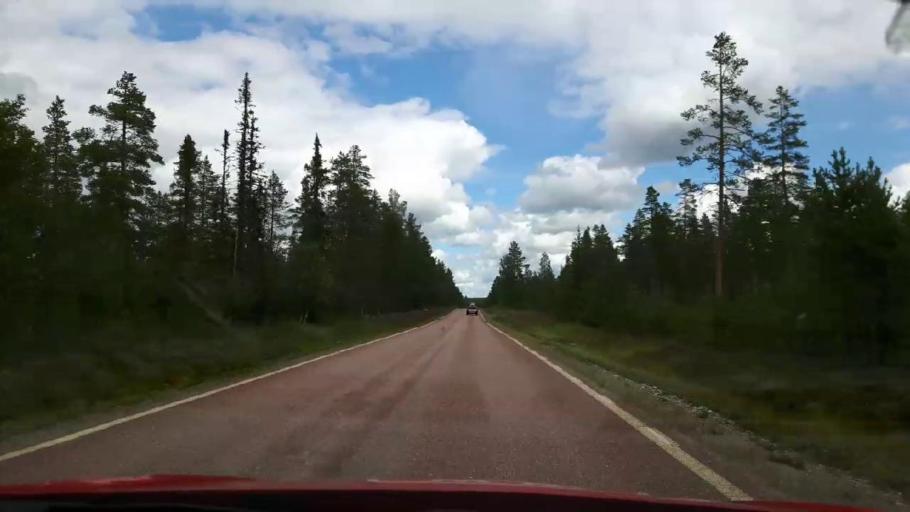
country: NO
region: Hedmark
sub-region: Trysil
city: Innbygda
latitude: 61.8840
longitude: 12.9756
